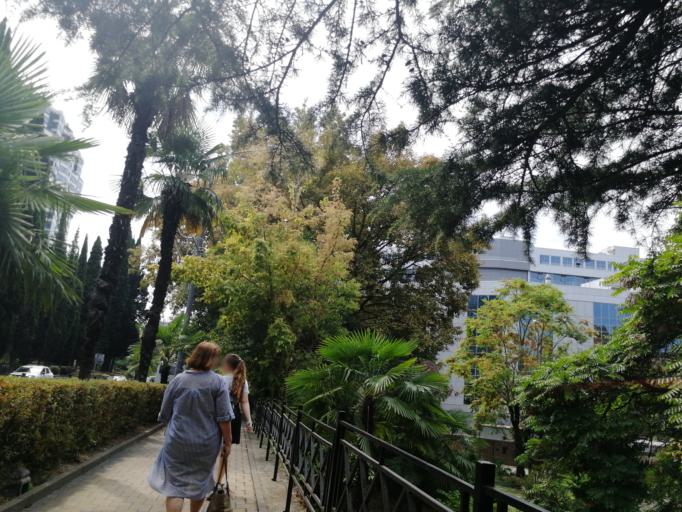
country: RU
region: Krasnodarskiy
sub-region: Sochi City
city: Sochi
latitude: 43.5845
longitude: 39.7236
